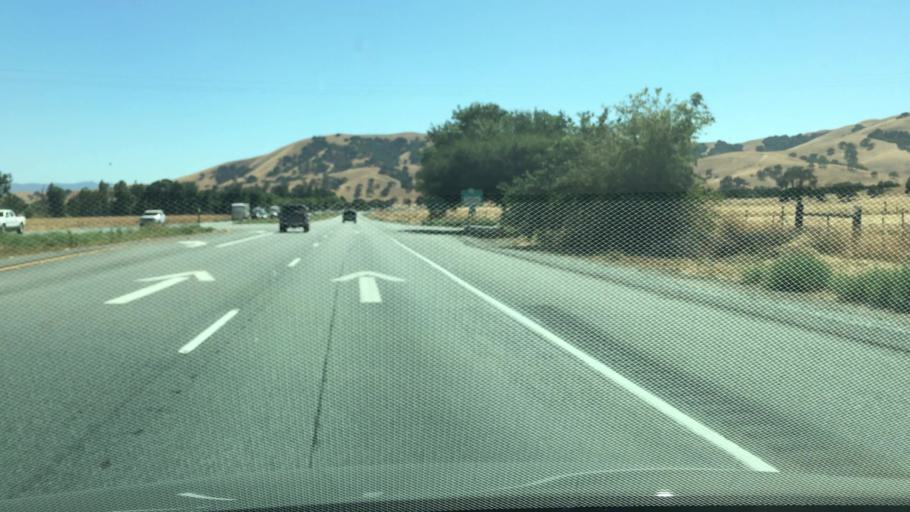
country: US
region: California
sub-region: San Benito County
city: Hollister
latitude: 37.0033
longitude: -121.3706
